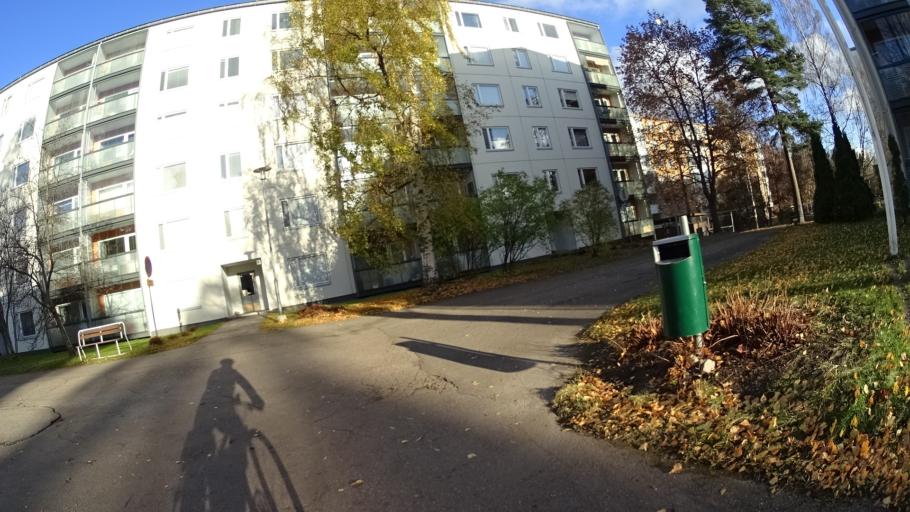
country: FI
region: Uusimaa
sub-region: Helsinki
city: Kilo
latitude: 60.2759
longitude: 24.8407
